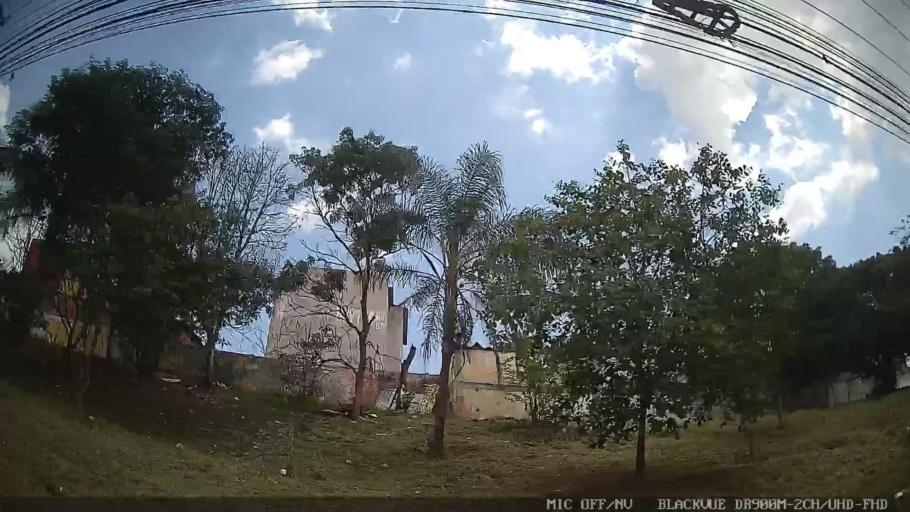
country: BR
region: Sao Paulo
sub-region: Taboao Da Serra
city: Taboao da Serra
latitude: -23.6619
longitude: -46.7792
